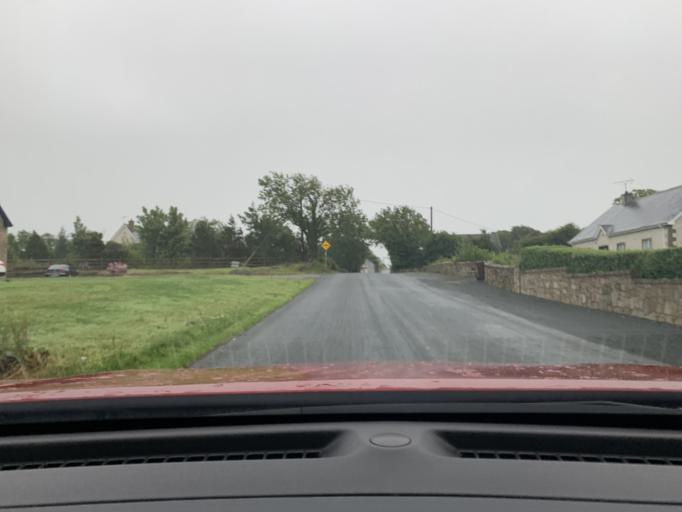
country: IE
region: Connaught
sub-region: County Leitrim
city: Kinlough
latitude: 54.4397
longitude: -8.4364
